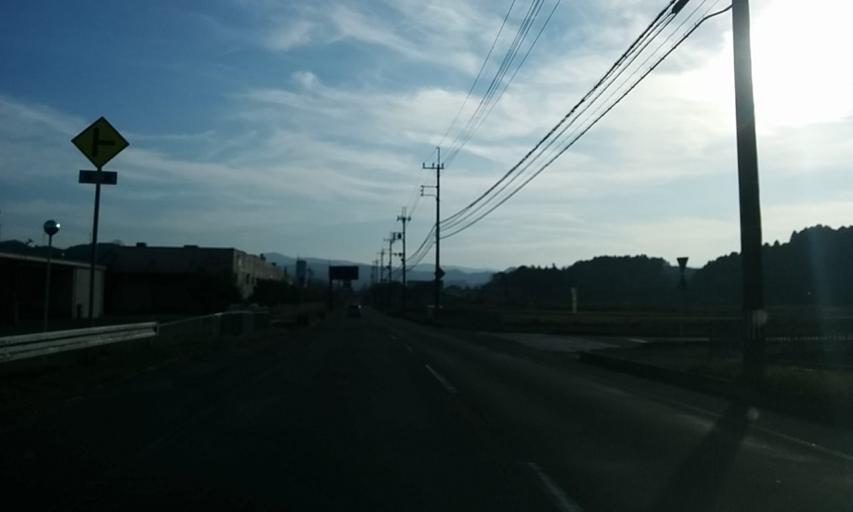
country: JP
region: Kyoto
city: Kameoka
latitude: 35.1281
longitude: 135.4839
